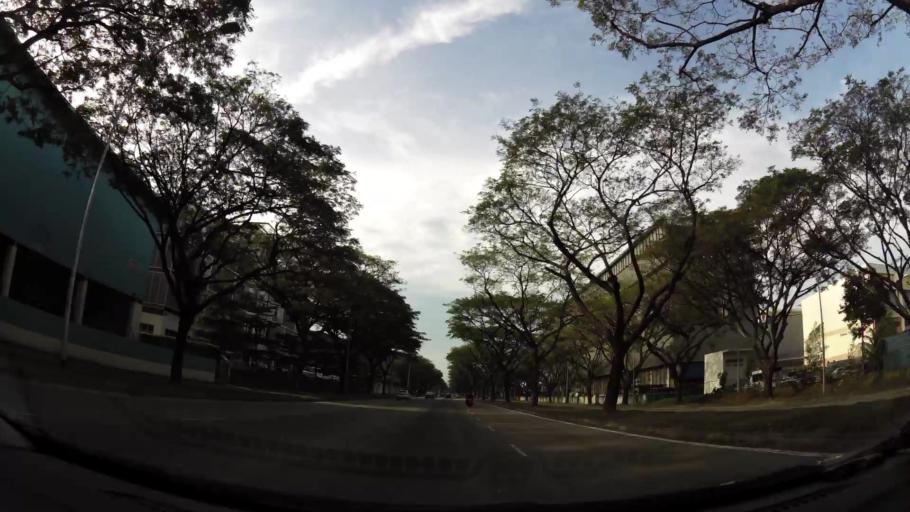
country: MY
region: Johor
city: Johor Bahru
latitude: 1.3164
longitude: 103.6296
